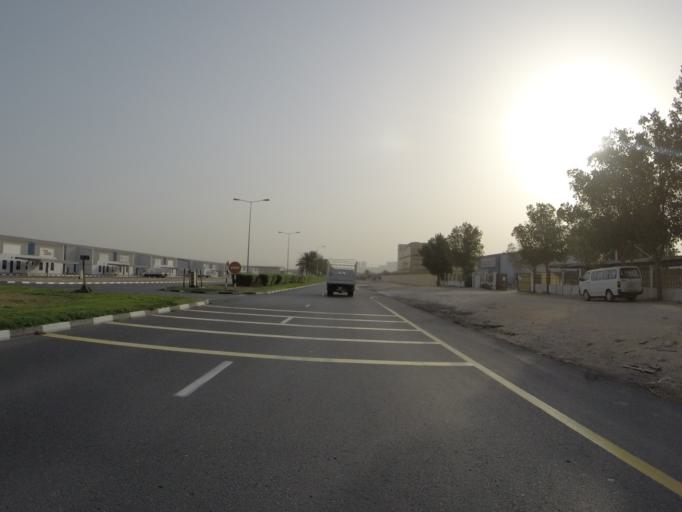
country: AE
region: Dubai
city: Dubai
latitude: 24.9632
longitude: 55.0684
